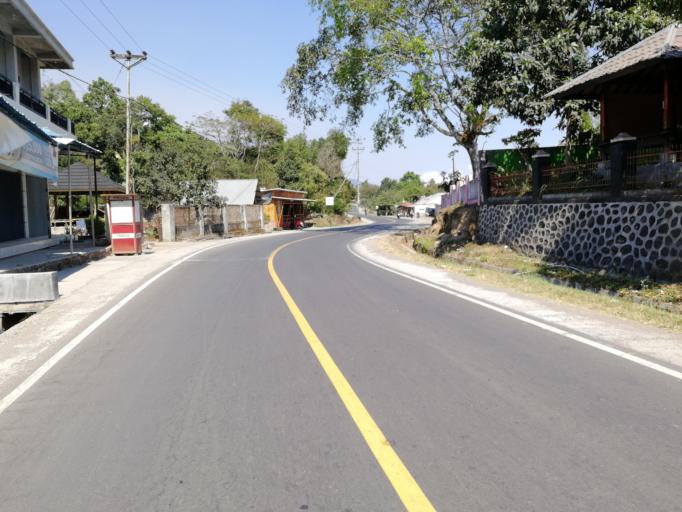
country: ID
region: West Nusa Tenggara
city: Sembalunlawang
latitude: -8.3601
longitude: 116.5324
